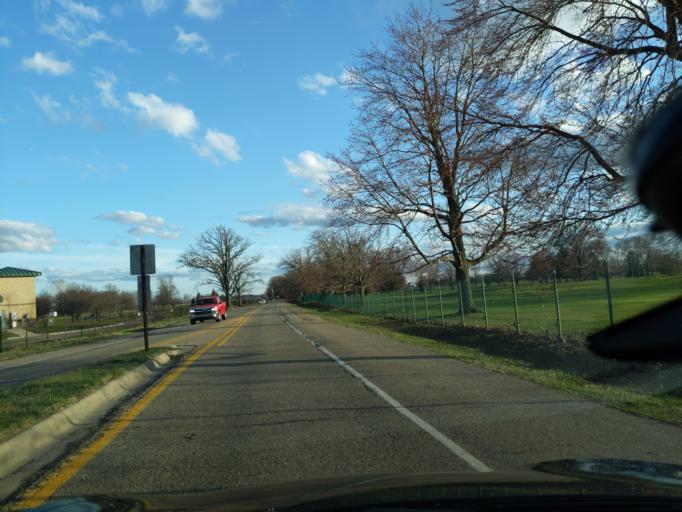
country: US
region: Michigan
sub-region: Ingham County
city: East Lansing
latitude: 42.7078
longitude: -84.4940
